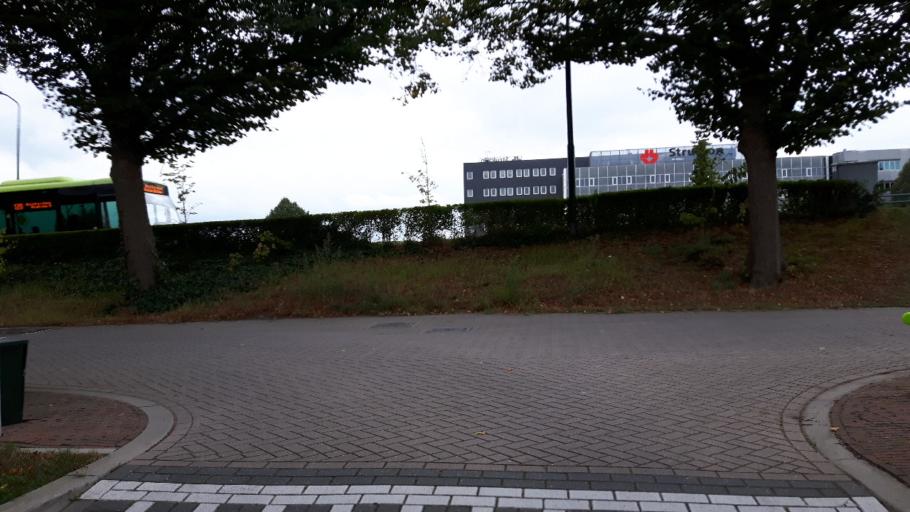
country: NL
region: Utrecht
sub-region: Stichtse Vecht
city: Maarssen
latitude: 52.1272
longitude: 5.0549
